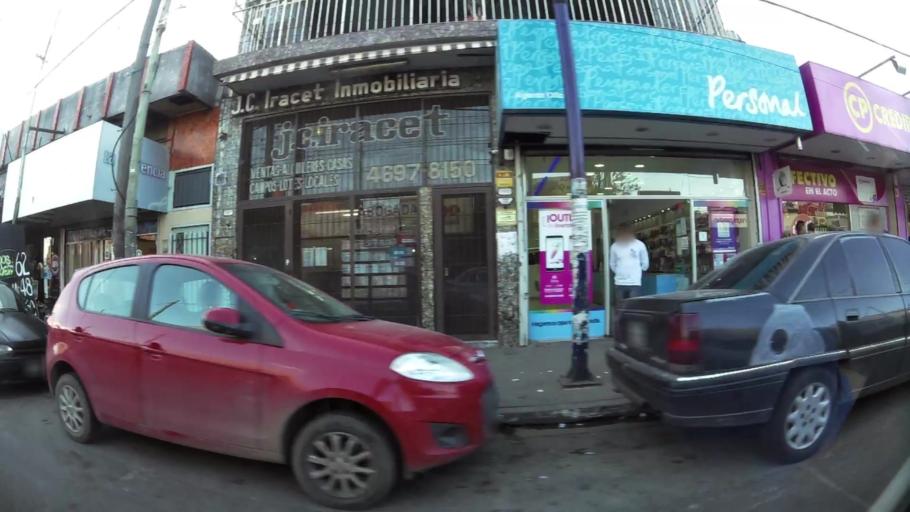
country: AR
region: Buenos Aires
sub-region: Partido de Moron
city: Moron
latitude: -34.6991
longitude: -58.6262
